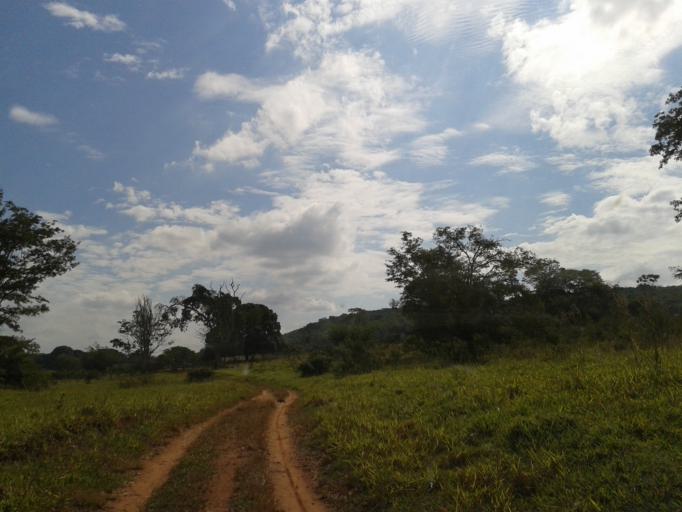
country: BR
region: Minas Gerais
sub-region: Campina Verde
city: Campina Verde
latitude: -19.3939
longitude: -49.6709
